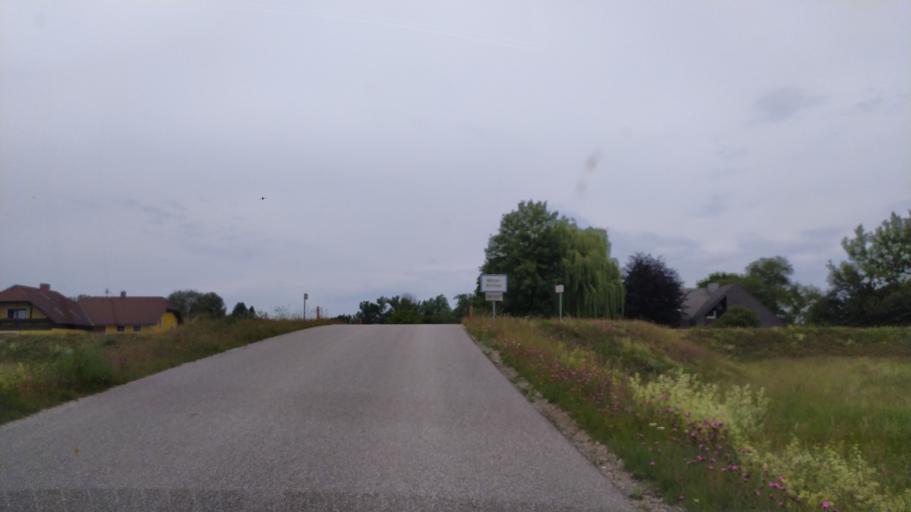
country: AT
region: Lower Austria
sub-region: Politischer Bezirk Amstetten
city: Strengberg
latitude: 48.1841
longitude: 14.6987
